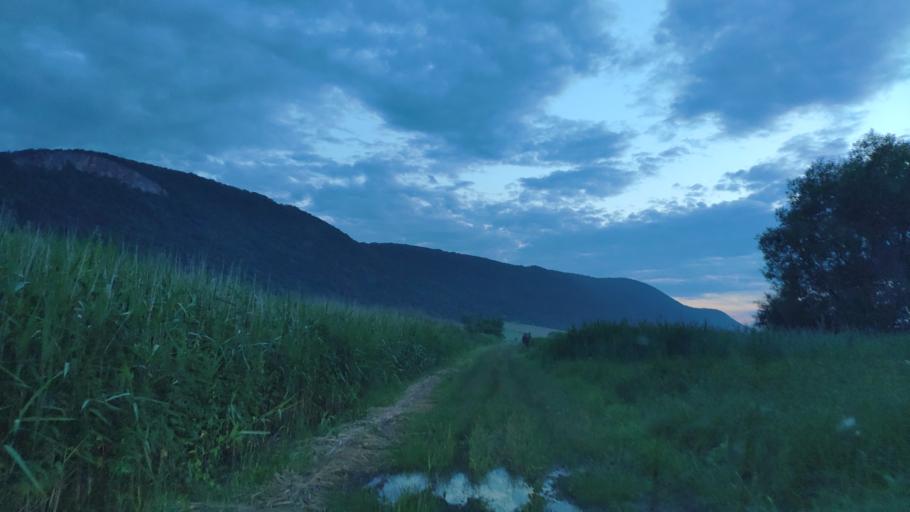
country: SK
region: Kosicky
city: Medzev
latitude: 48.5849
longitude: 20.8090
